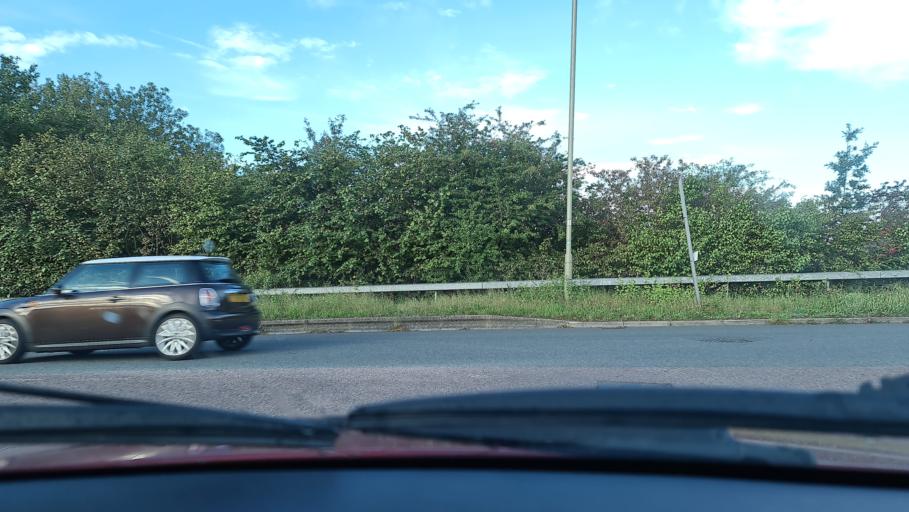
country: GB
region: England
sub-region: Oxfordshire
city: Kidlington
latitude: 51.8273
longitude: -1.3030
